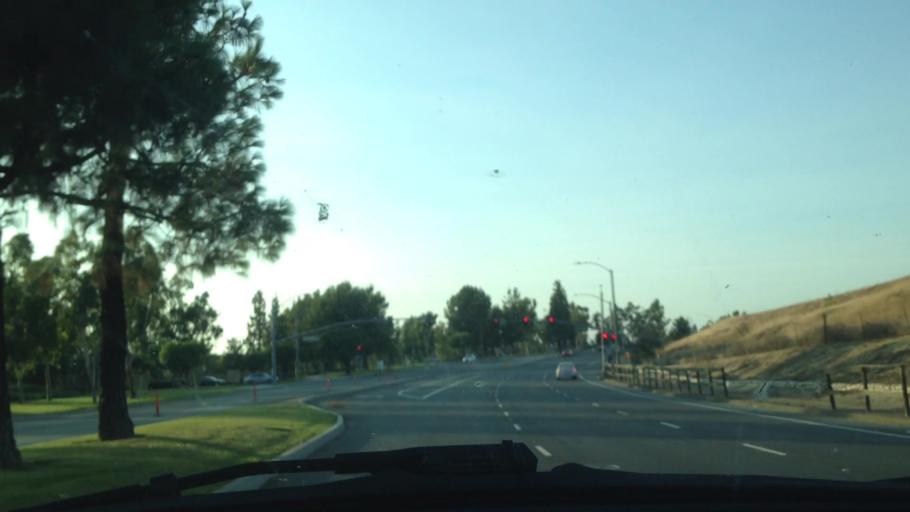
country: US
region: California
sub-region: Orange County
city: North Tustin
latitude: 33.7889
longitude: -117.7607
